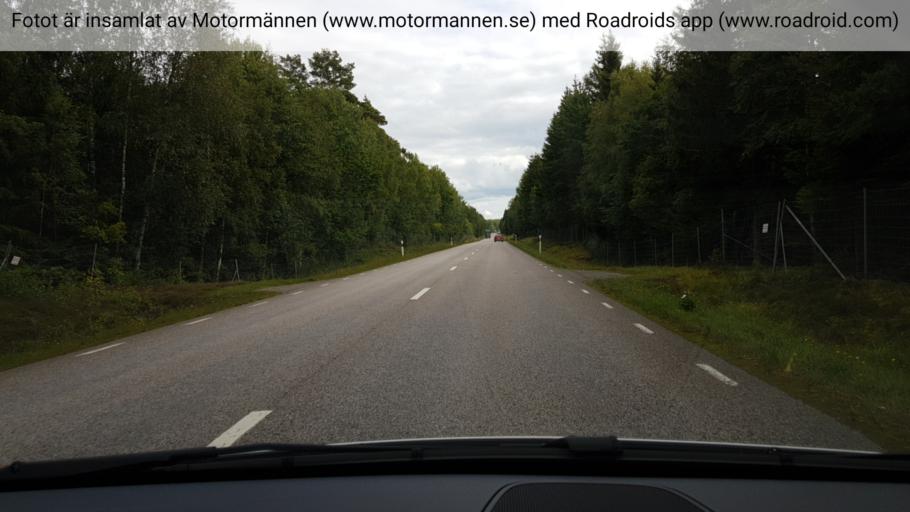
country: SE
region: Vaestra Goetaland
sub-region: Falkopings Kommun
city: Floby
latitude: 58.2089
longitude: 13.2746
